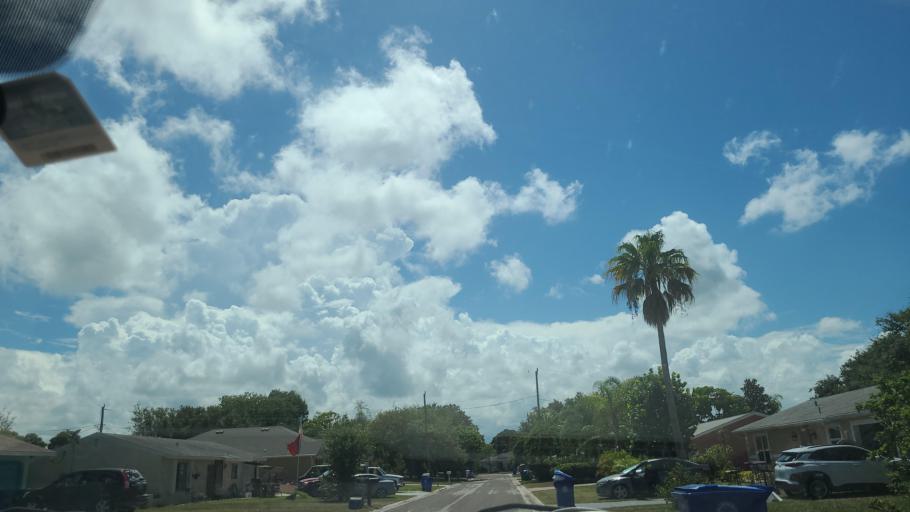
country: US
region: Florida
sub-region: Indian River County
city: Sebastian
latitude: 27.7773
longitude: -80.4608
